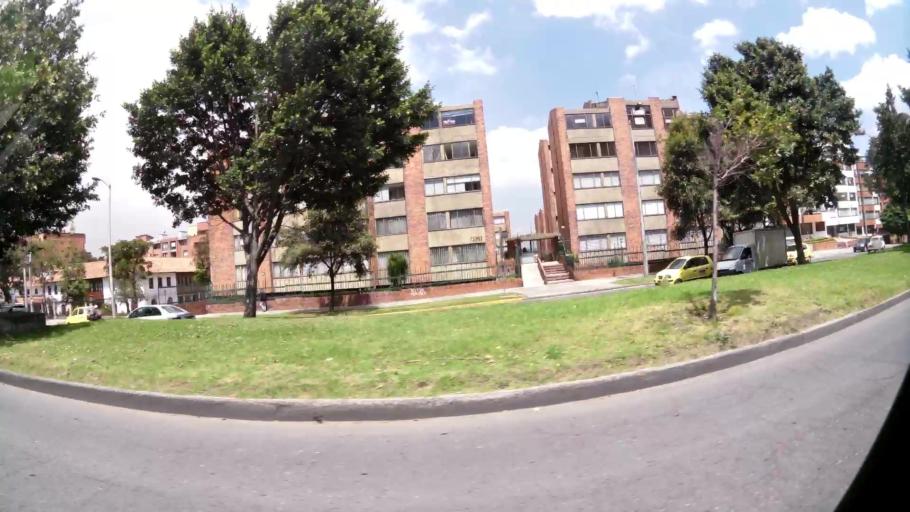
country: CO
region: Cundinamarca
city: La Calera
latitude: 4.7255
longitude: -74.0247
